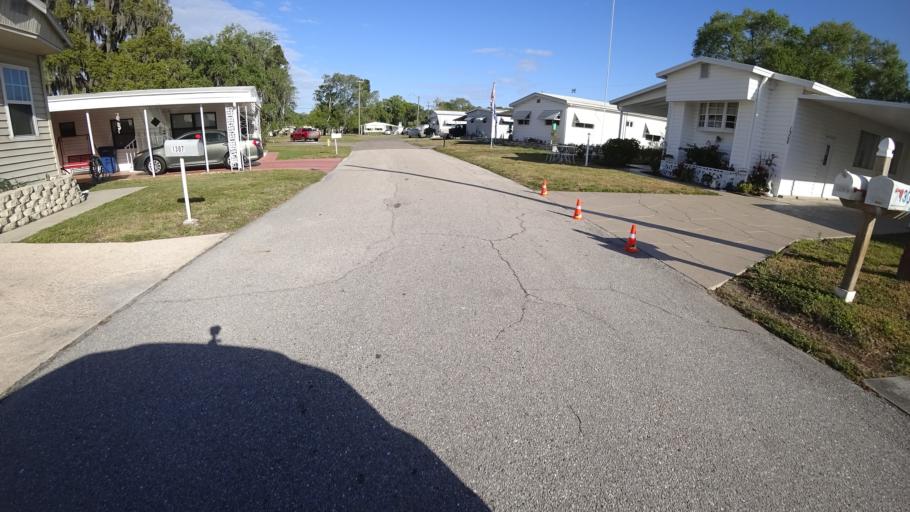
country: US
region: Florida
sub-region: Manatee County
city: Ellenton
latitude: 27.5253
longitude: -82.5232
